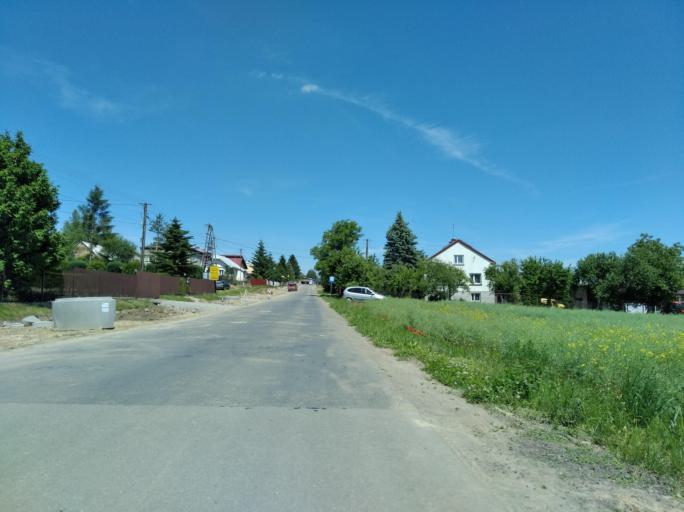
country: PL
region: Subcarpathian Voivodeship
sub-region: Powiat jasielski
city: Tarnowiec
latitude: 49.7081
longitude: 21.5533
